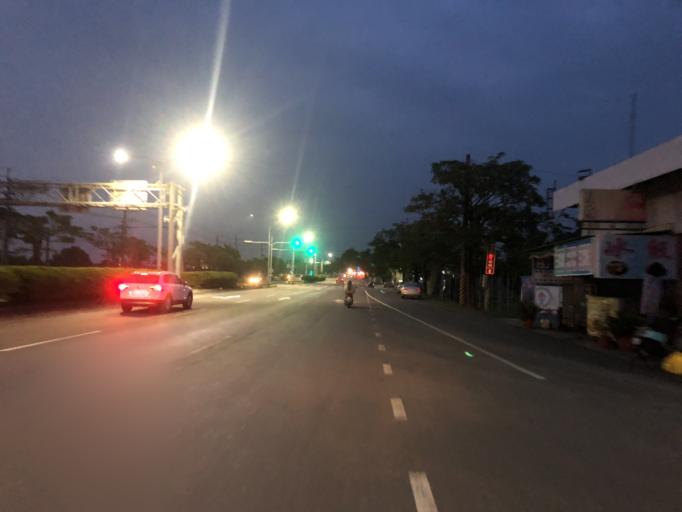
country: TW
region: Taiwan
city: Yujing
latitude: 23.1640
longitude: 120.3410
